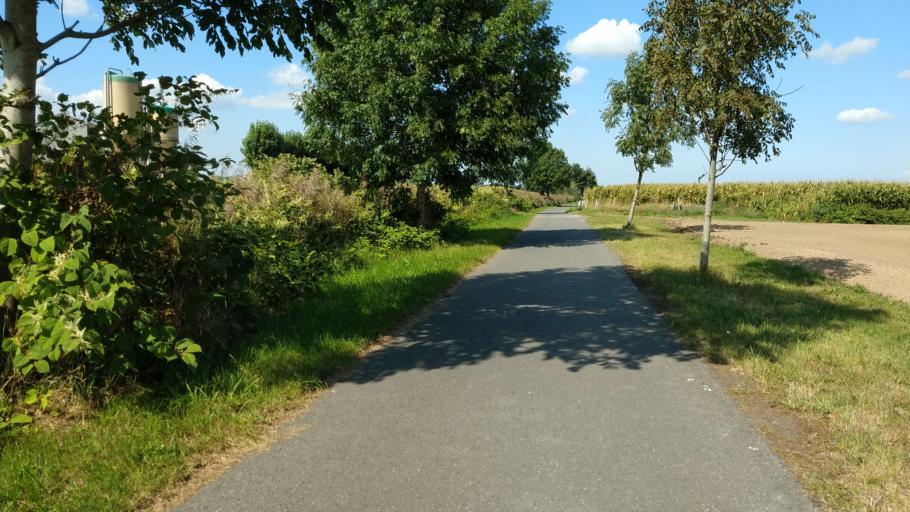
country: BE
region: Flanders
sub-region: Provincie Oost-Vlaanderen
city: Assenede
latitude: 51.2401
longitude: 3.7217
